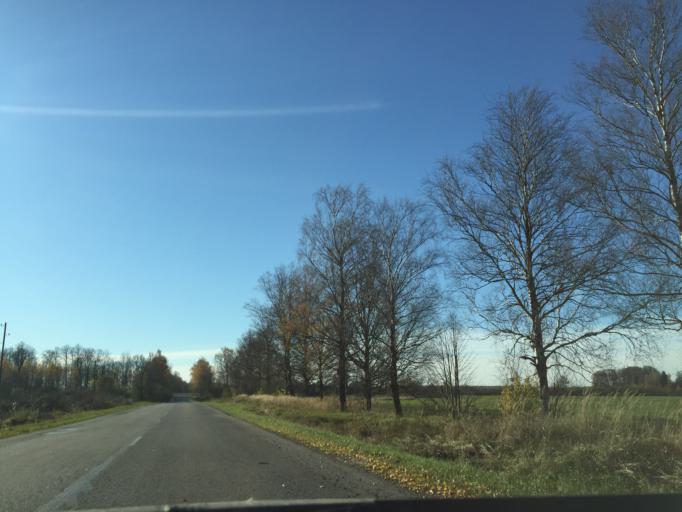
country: LV
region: Skriveri
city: Skriveri
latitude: 56.6877
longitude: 25.1458
